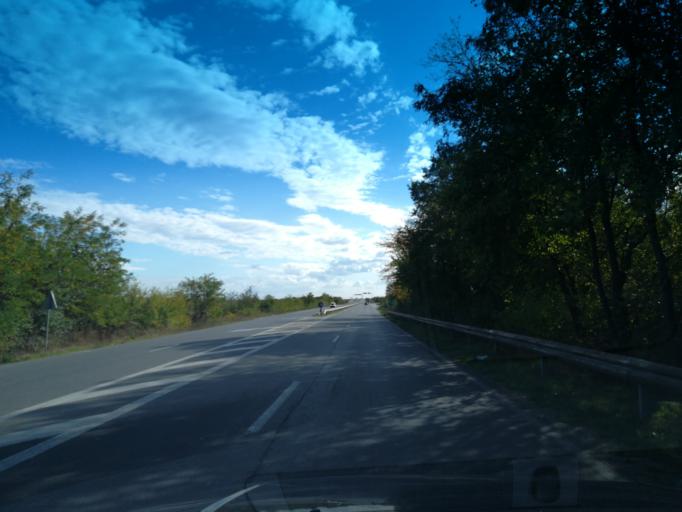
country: BG
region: Stara Zagora
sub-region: Obshtina Stara Zagora
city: Stara Zagora
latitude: 42.3458
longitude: 25.6601
